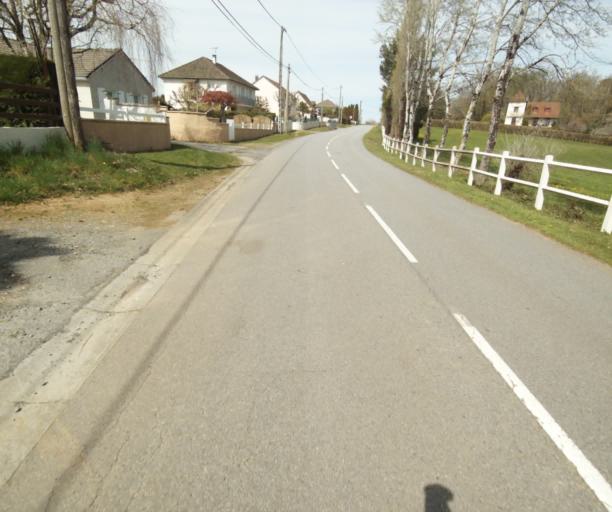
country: FR
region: Limousin
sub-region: Departement de la Correze
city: Correze
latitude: 45.3765
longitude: 1.8031
